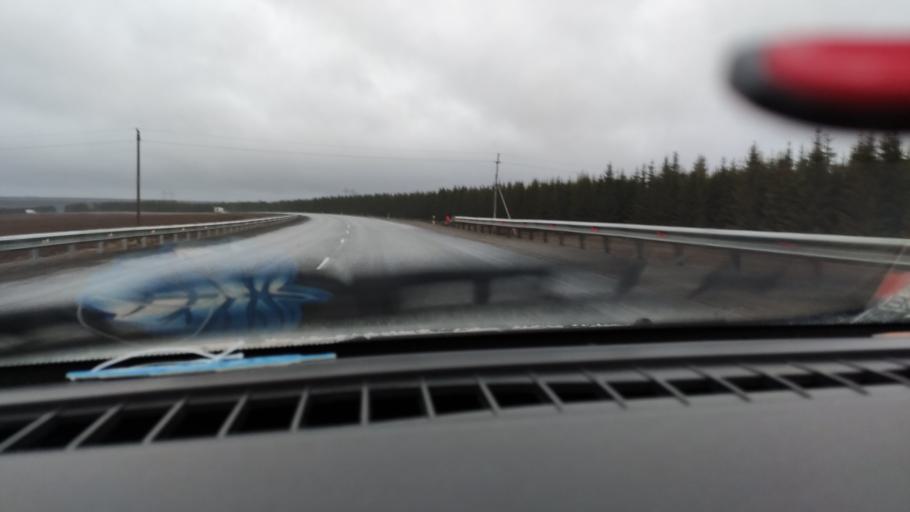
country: RU
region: Udmurtiya
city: Alnashi
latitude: 56.0819
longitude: 52.4057
